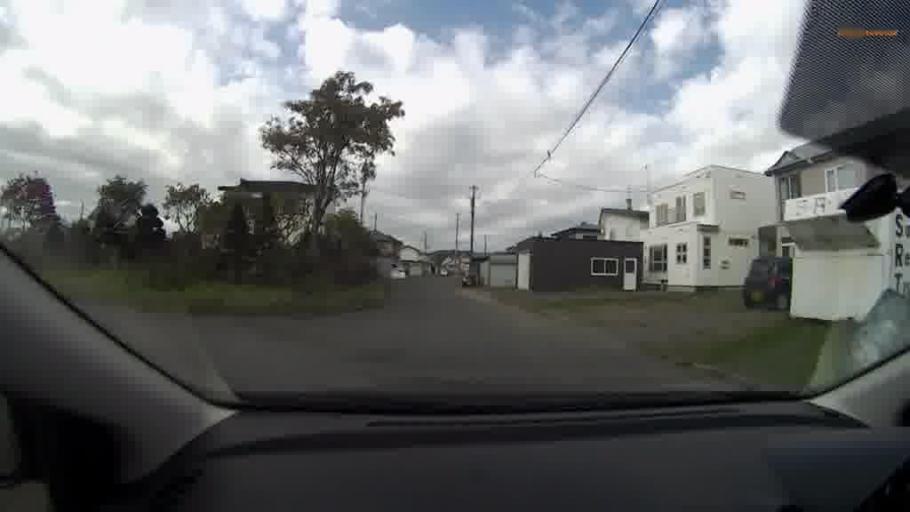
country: JP
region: Hokkaido
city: Kushiro
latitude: 42.9766
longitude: 144.1293
